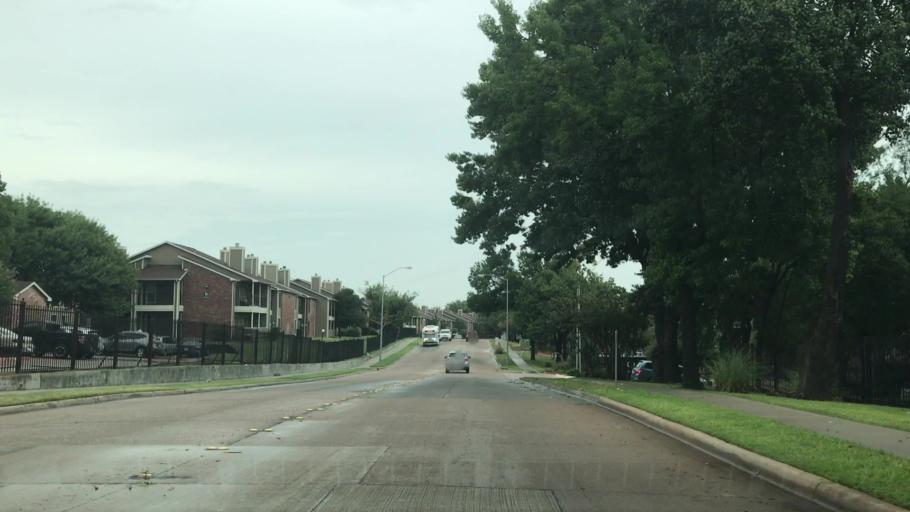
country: US
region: Texas
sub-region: Denton County
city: Lewisville
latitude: 33.0191
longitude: -96.9908
